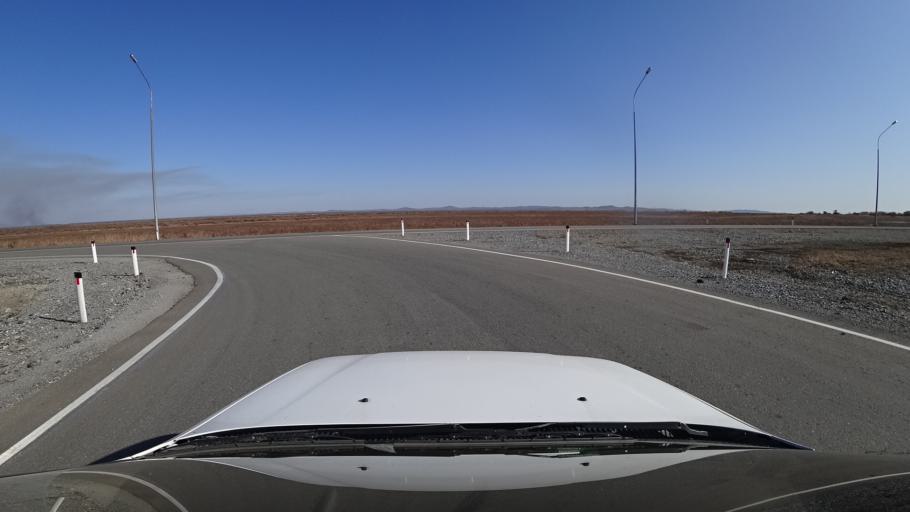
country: RU
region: Primorskiy
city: Lazo
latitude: 45.8631
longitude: 133.7196
